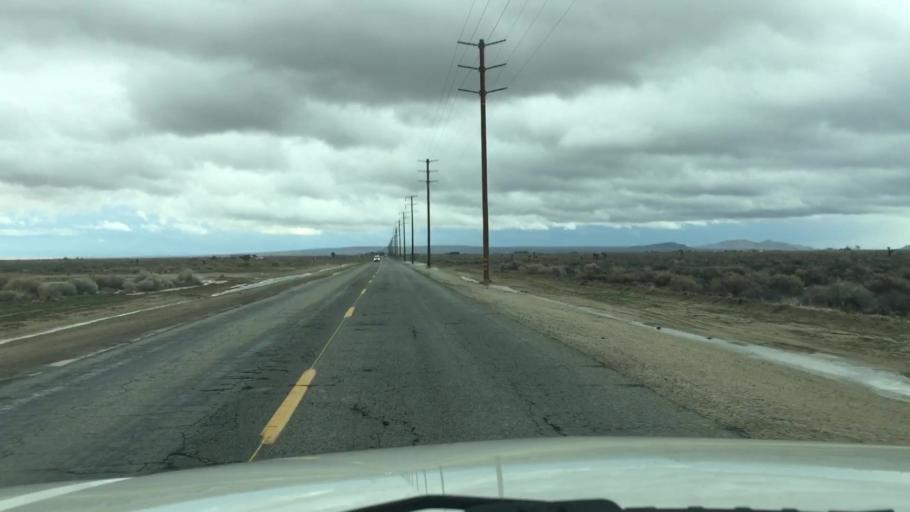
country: US
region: California
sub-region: Los Angeles County
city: Lancaster
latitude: 34.7631
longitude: -118.0576
